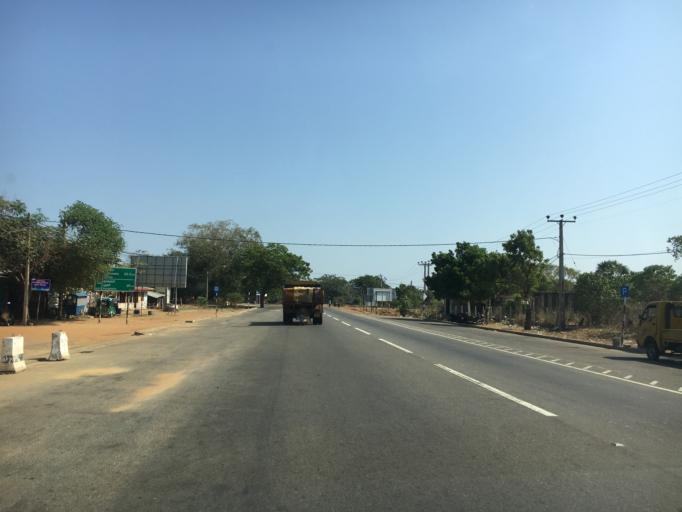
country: LK
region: Northern Province
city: Kilinochchi
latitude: 9.4368
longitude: 80.4076
